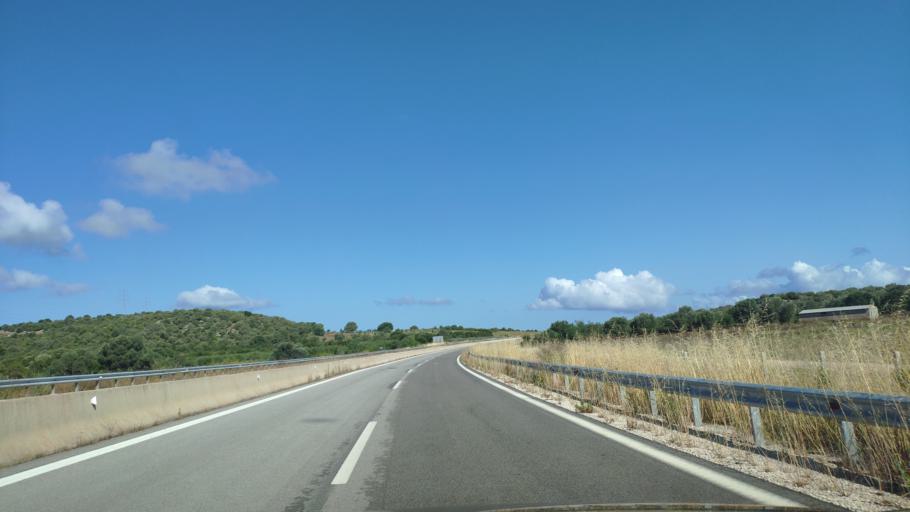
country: GR
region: West Greece
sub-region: Nomos Aitolias kai Akarnanias
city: Vonitsa
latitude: 38.9047
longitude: 20.8535
